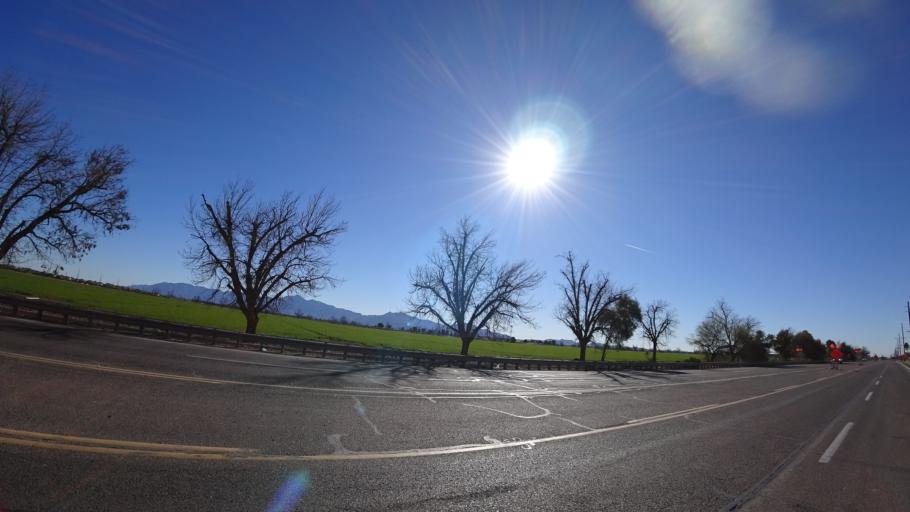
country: US
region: Arizona
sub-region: Maricopa County
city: Tolleson
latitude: 33.4358
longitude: -112.2577
